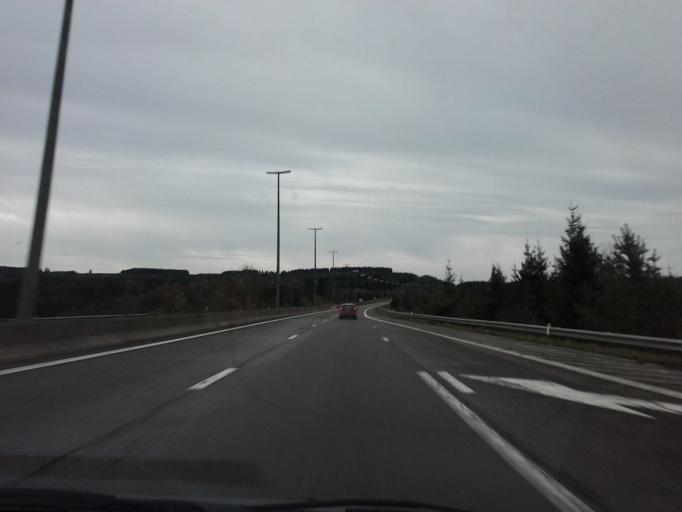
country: BE
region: Wallonia
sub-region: Province du Luxembourg
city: Manhay
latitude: 50.3120
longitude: 5.7105
